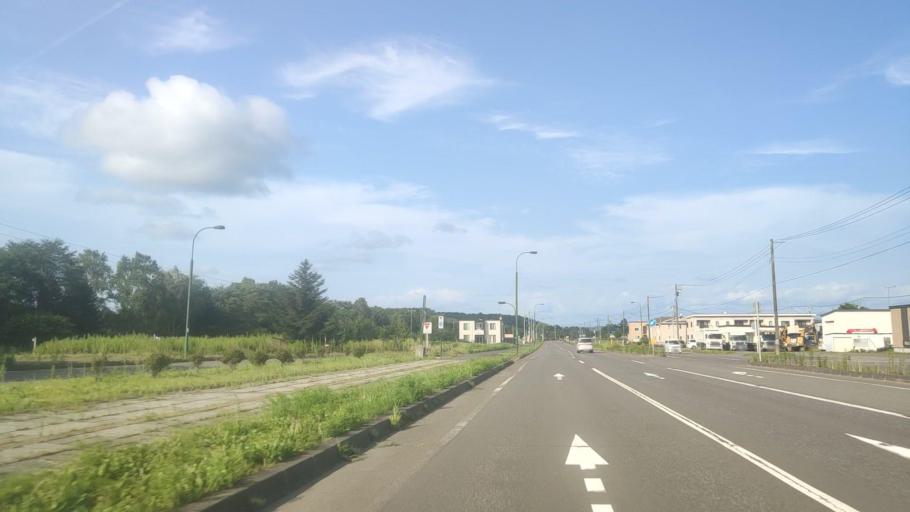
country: JP
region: Hokkaido
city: Chitose
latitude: 42.7657
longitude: 141.8153
